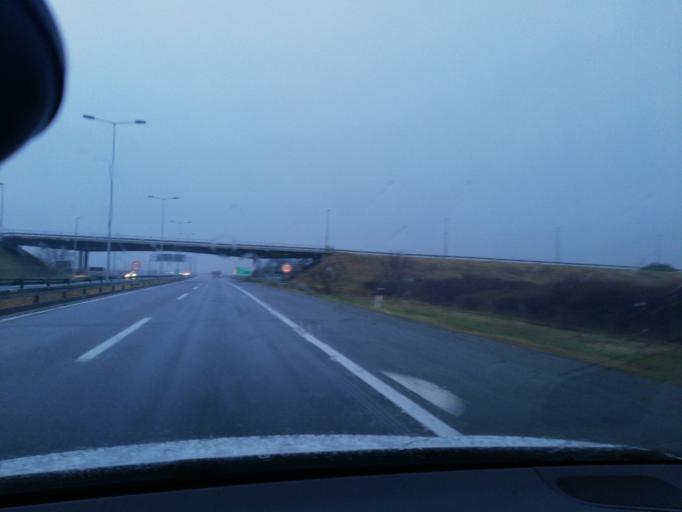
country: RS
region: Autonomna Pokrajina Vojvodina
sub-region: Sremski Okrug
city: Ruma
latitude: 44.9632
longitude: 19.8074
